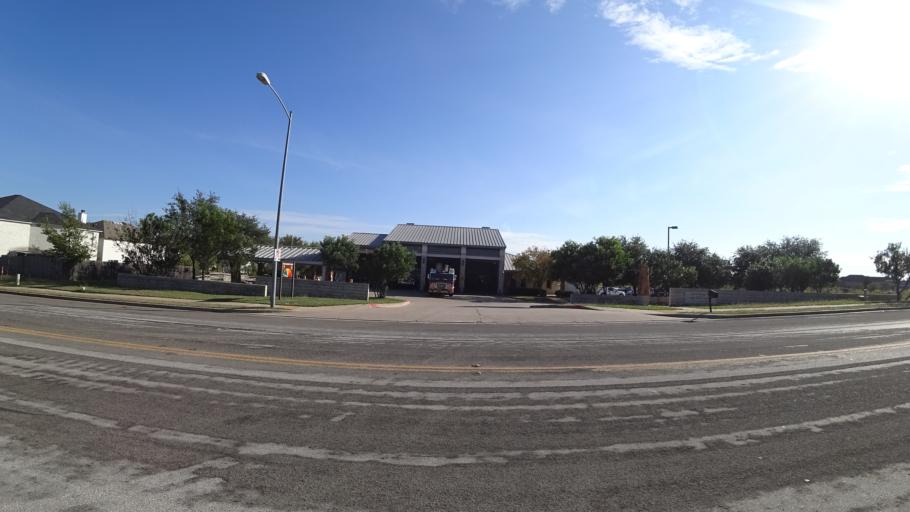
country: US
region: Texas
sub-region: Travis County
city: Pflugerville
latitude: 30.3999
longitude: -97.6534
